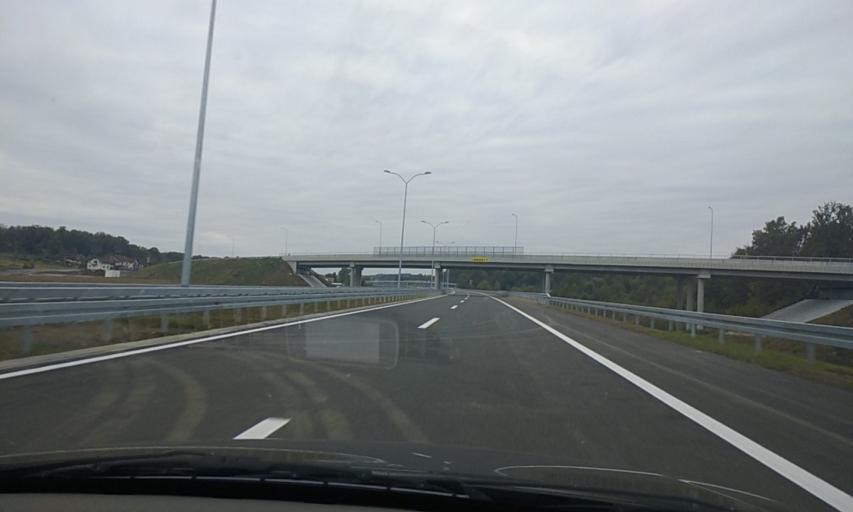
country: BA
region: Republika Srpska
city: Prnjavor
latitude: 44.8901
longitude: 17.5717
